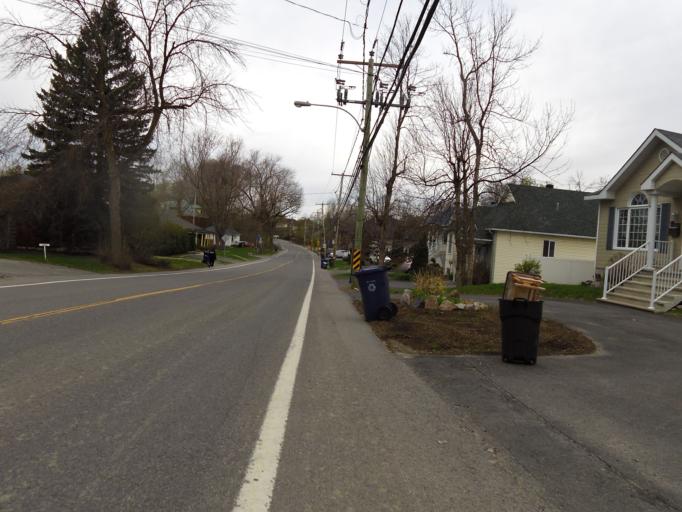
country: CA
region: Quebec
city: Dollard-Des Ormeaux
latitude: 45.5199
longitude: -73.8082
